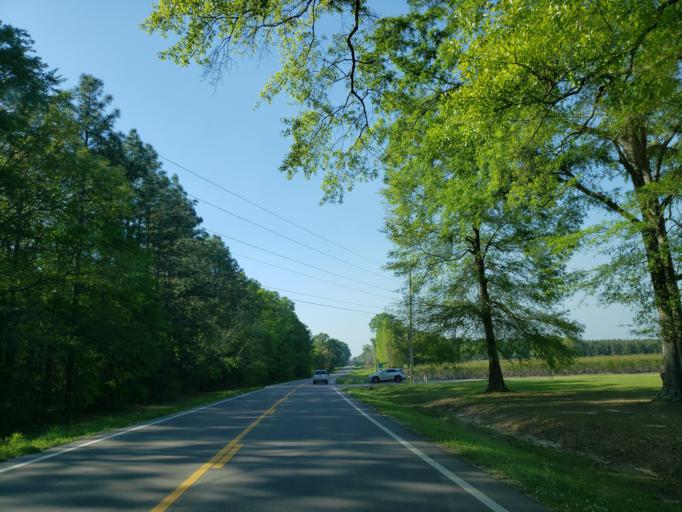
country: US
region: Mississippi
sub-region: Perry County
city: Richton
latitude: 31.4090
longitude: -88.9527
